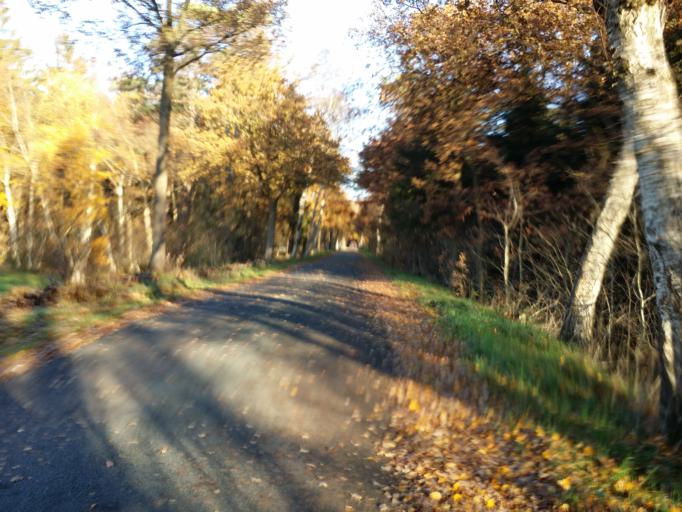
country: DE
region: Lower Saxony
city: Langwedel
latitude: 53.0289
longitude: 9.1853
